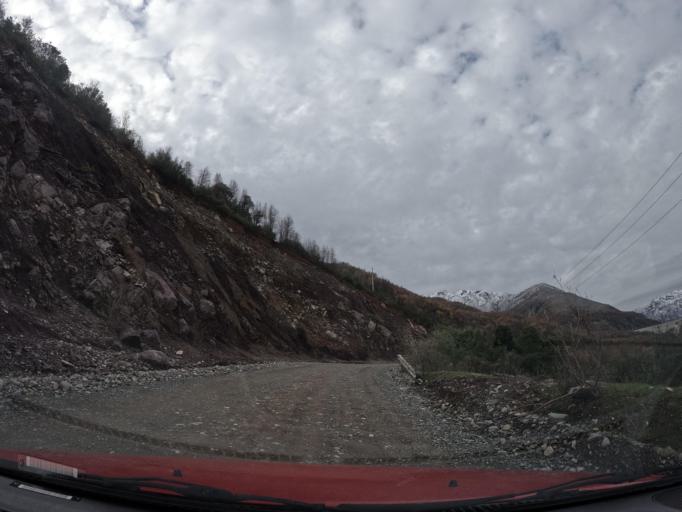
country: CL
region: Maule
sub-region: Provincia de Linares
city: Colbun
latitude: -35.8565
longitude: -71.2077
